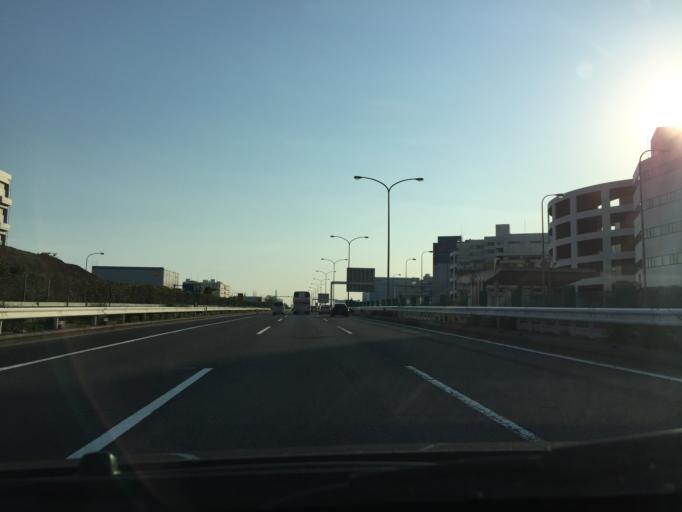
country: JP
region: Kanagawa
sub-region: Kawasaki-shi
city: Kawasaki
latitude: 35.5013
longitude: 139.7656
